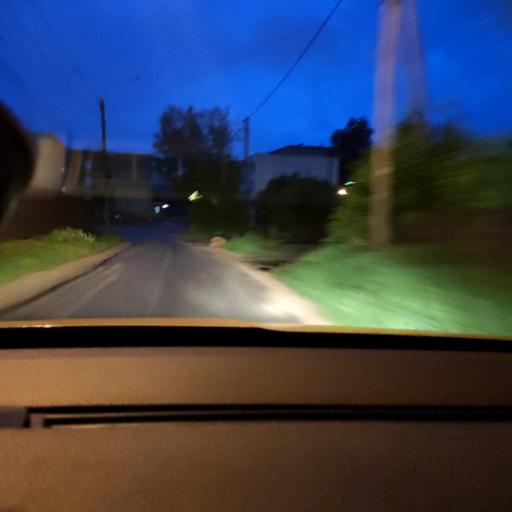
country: RU
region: Moskovskaya
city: Dmitrov
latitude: 56.3458
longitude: 37.5372
